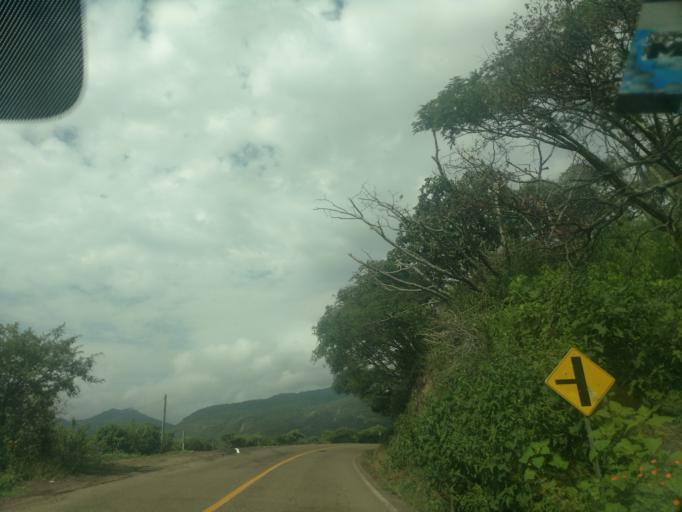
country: MX
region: Jalisco
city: El Salto
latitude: 20.3619
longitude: -104.5855
